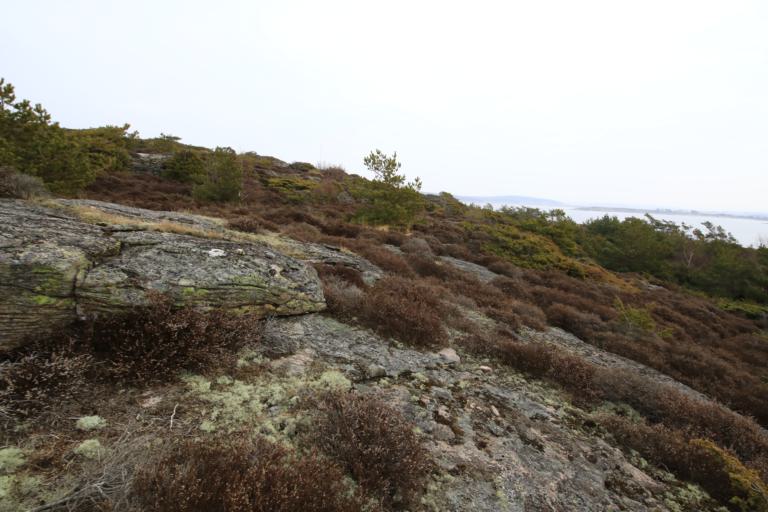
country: SE
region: Halland
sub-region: Kungsbacka Kommun
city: Frillesas
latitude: 57.2475
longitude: 12.1004
